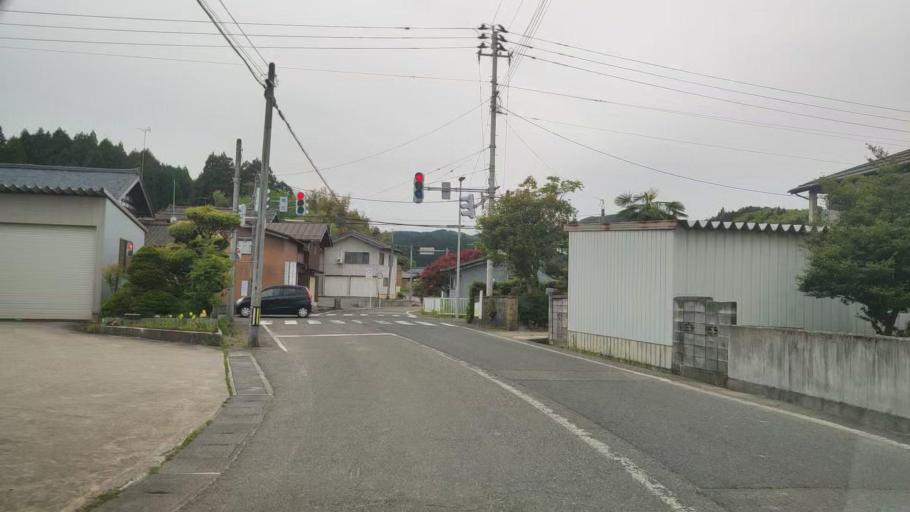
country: JP
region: Niigata
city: Gosen
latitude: 37.7255
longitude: 139.1372
